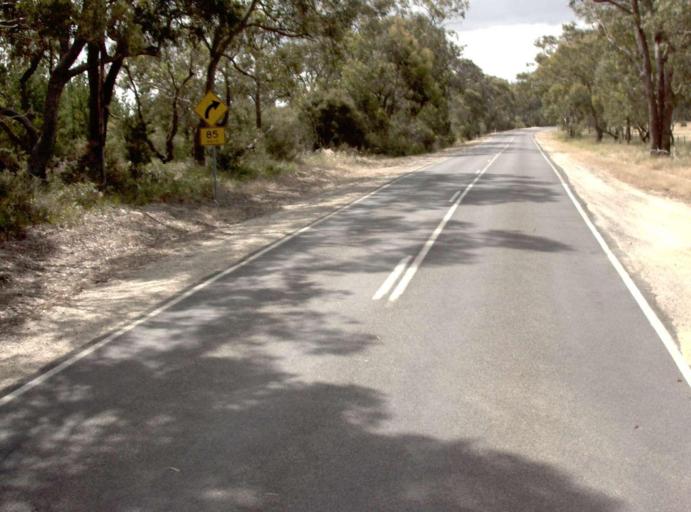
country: AU
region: Victoria
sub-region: Wellington
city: Sale
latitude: -38.2520
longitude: 147.1343
